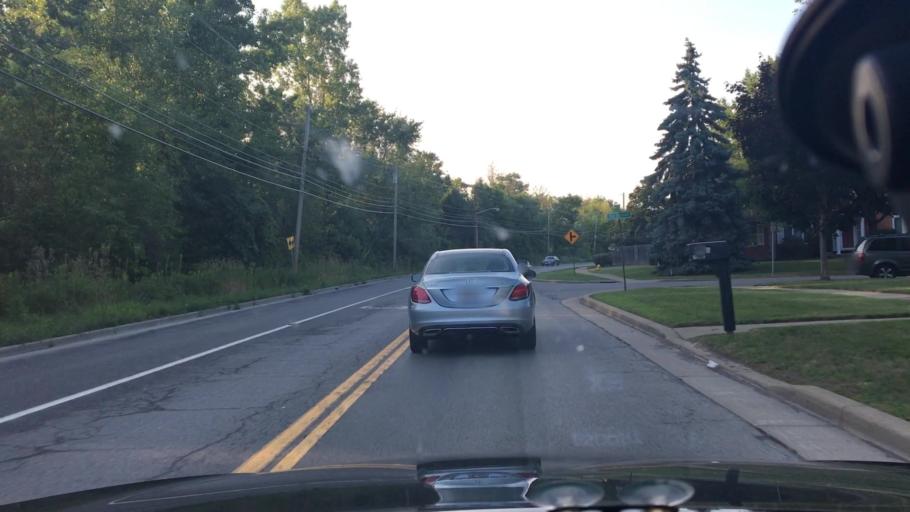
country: US
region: New York
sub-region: Erie County
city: Williamsville
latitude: 42.9981
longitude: -78.7608
